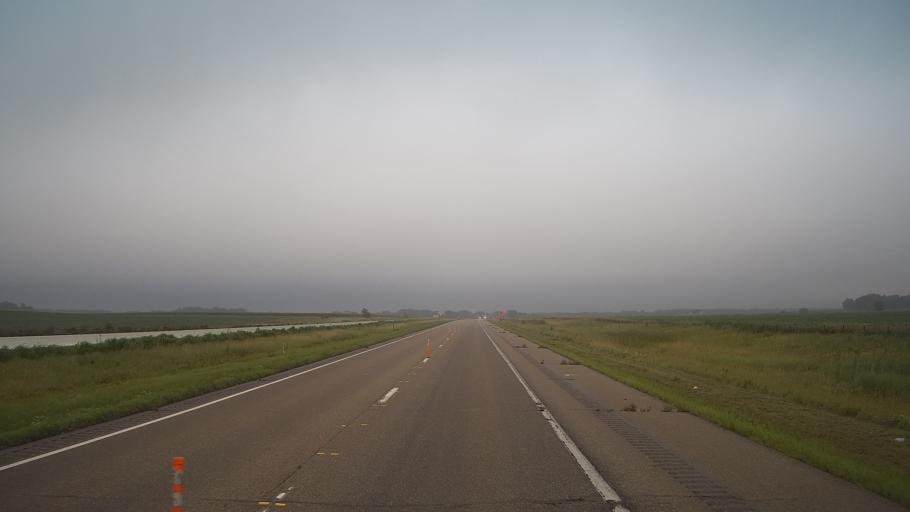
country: US
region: Minnesota
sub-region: Faribault County
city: Blue Earth
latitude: 43.6662
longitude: -94.1538
